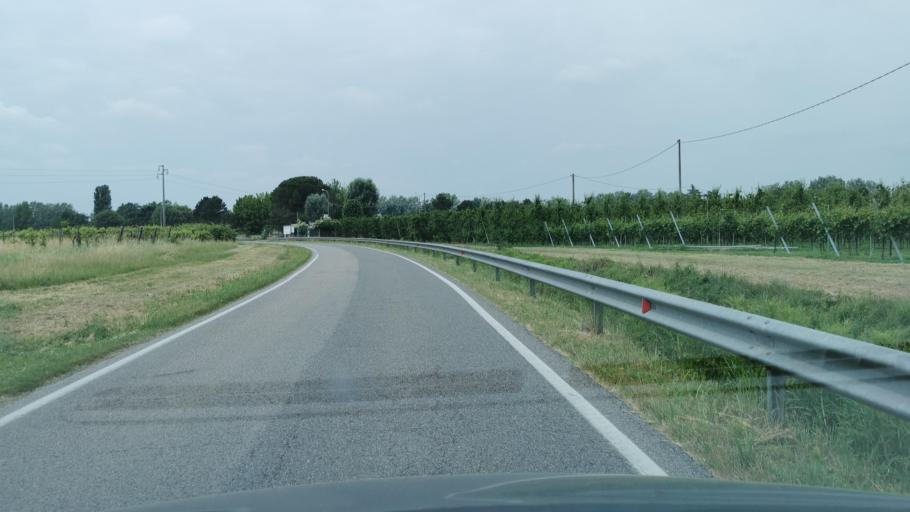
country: IT
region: Emilia-Romagna
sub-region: Provincia di Ravenna
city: Bagnacavallo
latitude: 44.4235
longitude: 11.9922
